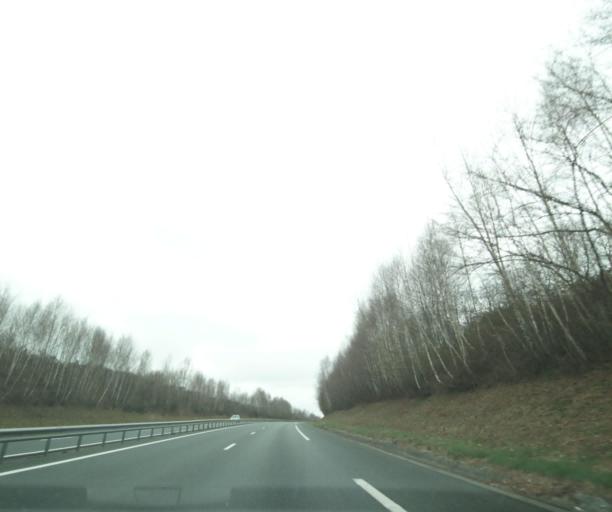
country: FR
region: Limousin
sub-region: Departement de la Haute-Vienne
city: Saint-Sulpice-les-Feuilles
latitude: 46.3732
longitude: 1.4441
